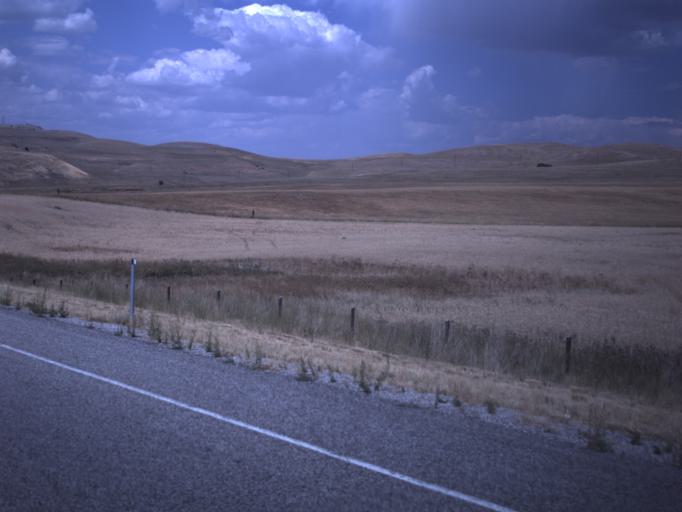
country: US
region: Utah
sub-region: Cache County
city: Mendon
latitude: 41.7811
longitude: -112.0237
